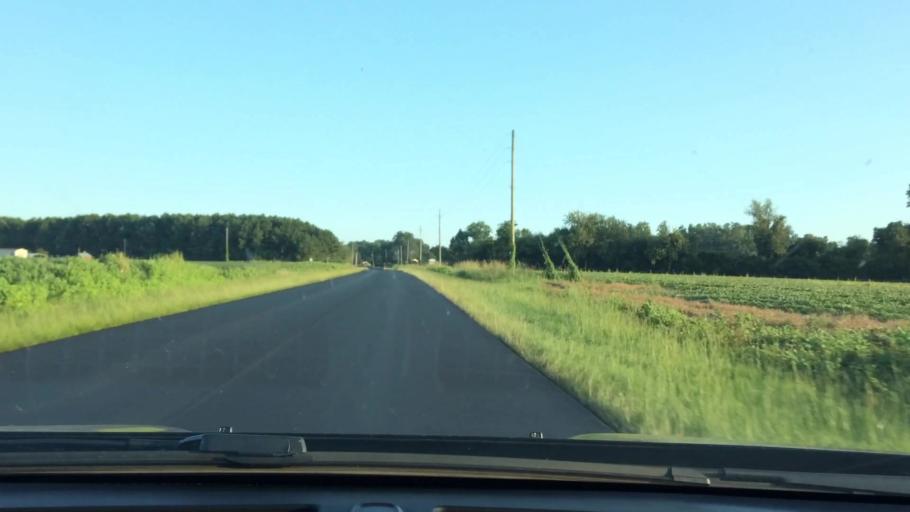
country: US
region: North Carolina
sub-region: Pitt County
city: Ayden
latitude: 35.4336
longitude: -77.4508
